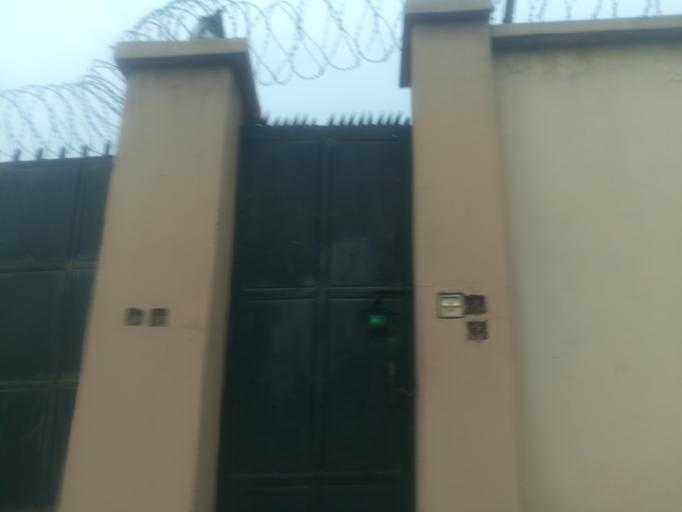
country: NG
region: Oyo
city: Ibadan
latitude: 7.4371
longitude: 3.9229
